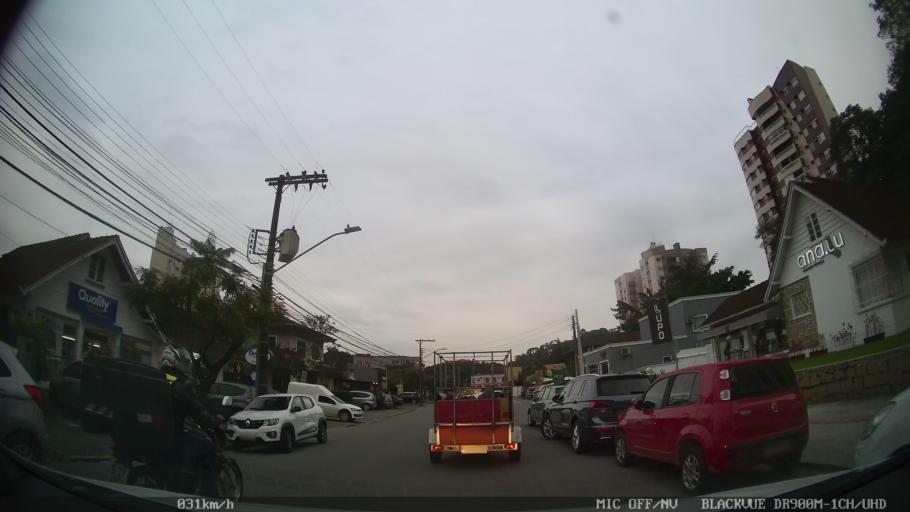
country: BR
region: Santa Catarina
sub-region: Joinville
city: Joinville
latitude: -26.3045
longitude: -48.8593
